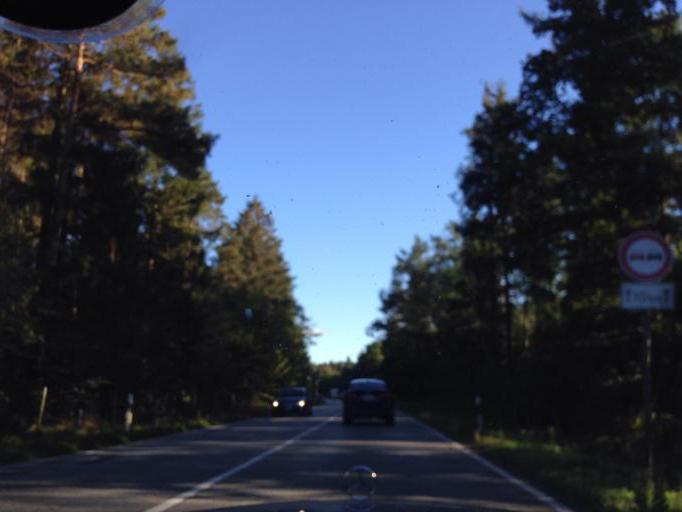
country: DE
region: Schleswig-Holstein
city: Boostedt
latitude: 54.0356
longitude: 10.0318
